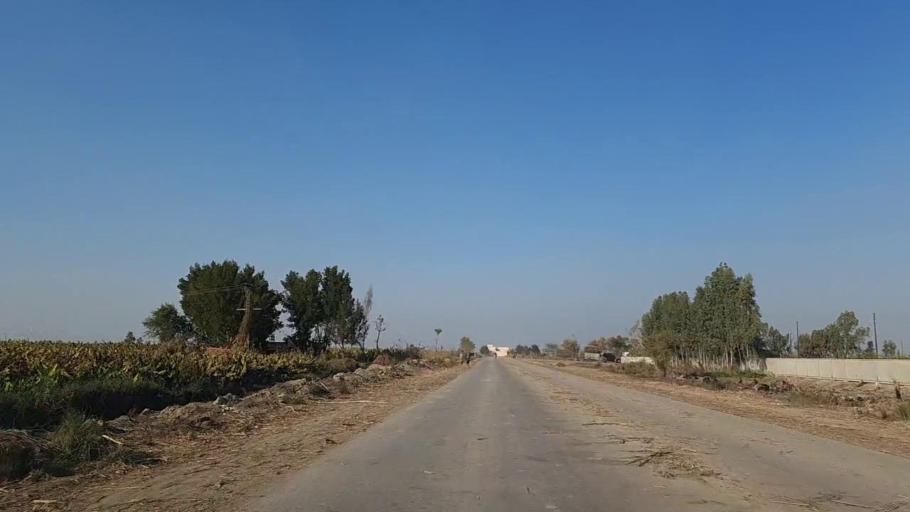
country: PK
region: Sindh
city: Bandhi
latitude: 26.6087
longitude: 68.3159
